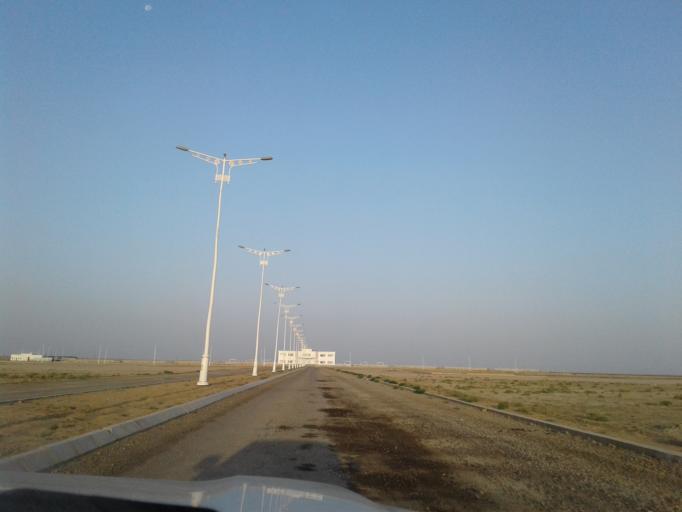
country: IR
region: Golestan
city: Aq Qayeh
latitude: 37.7059
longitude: 54.7481
